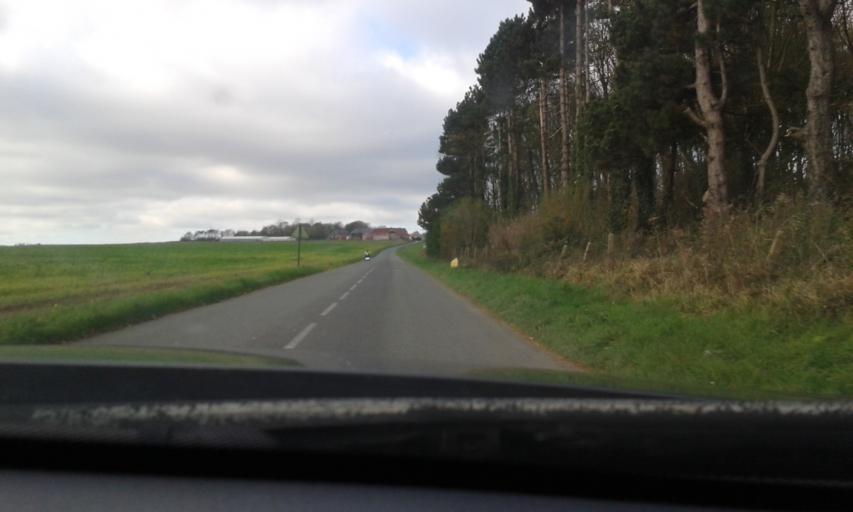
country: FR
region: Nord-Pas-de-Calais
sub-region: Departement du Pas-de-Calais
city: Ferques
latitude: 50.8770
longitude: 1.7690
